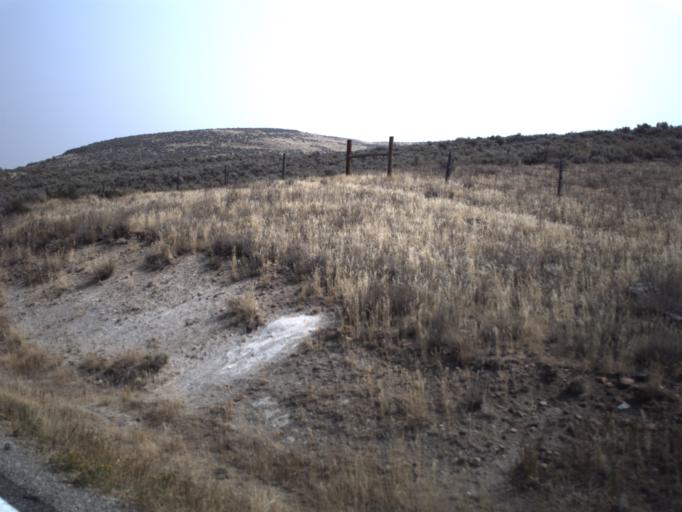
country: US
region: Utah
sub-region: Morgan County
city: Morgan
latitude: 40.9575
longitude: -111.5487
